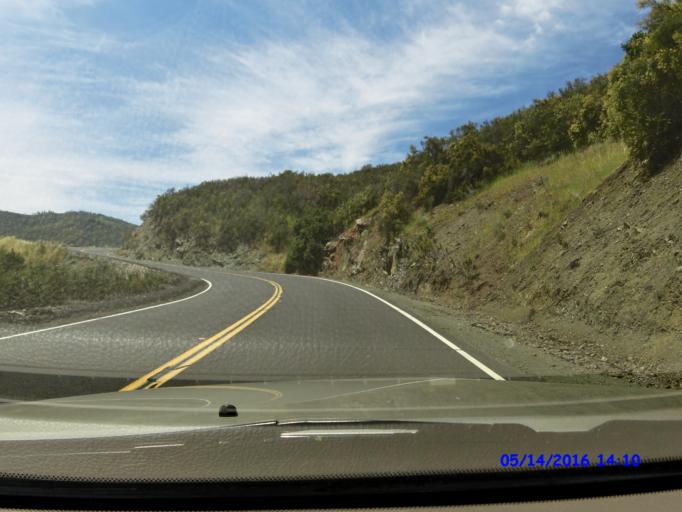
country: US
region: California
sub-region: Mariposa County
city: Mariposa
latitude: 37.6285
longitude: -120.1499
